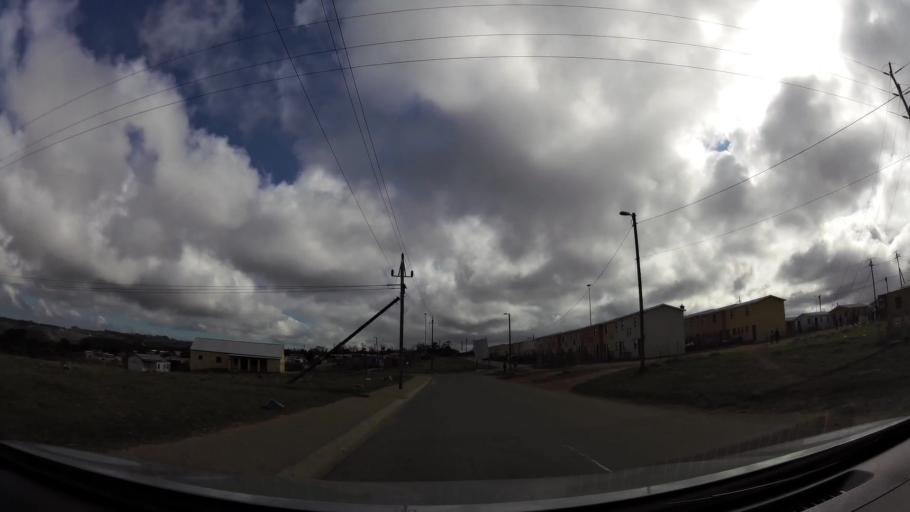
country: ZA
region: Western Cape
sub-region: Eden District Municipality
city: Plettenberg Bay
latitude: -34.0545
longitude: 23.3140
